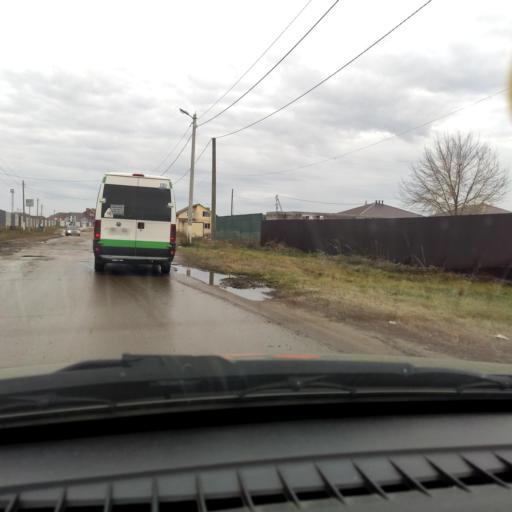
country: RU
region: Samara
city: Podstepki
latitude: 53.5147
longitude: 49.2216
